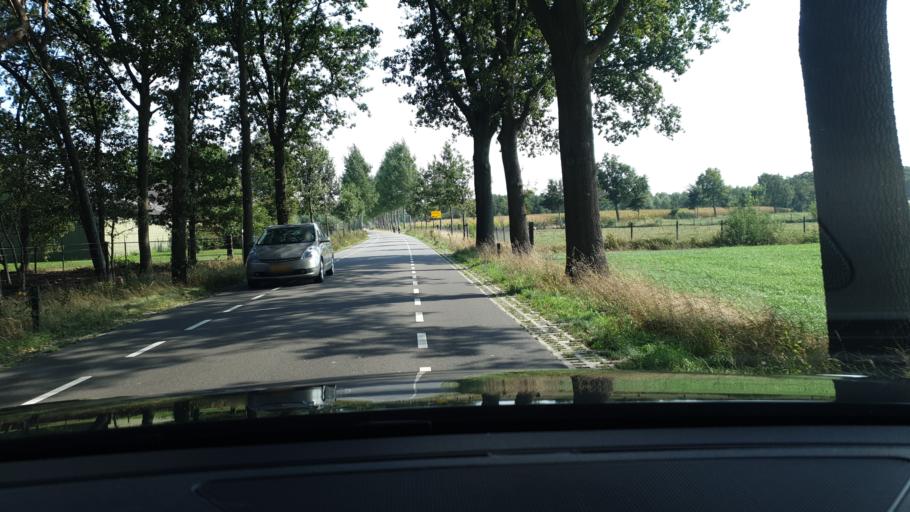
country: NL
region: North Brabant
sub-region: Gemeente Son en Breugel
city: Breugel
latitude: 51.5207
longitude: 5.5557
